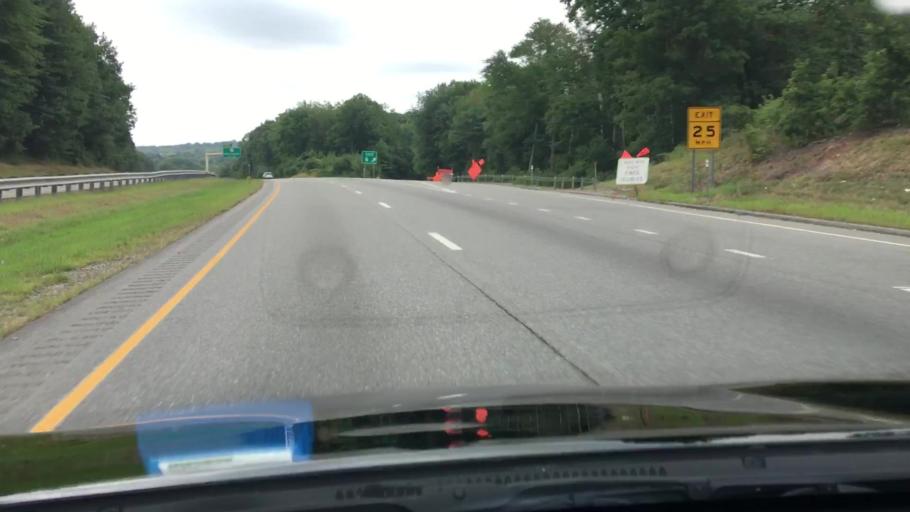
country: US
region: Connecticut
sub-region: New London County
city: Oxoboxo River
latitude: 41.4477
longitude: -72.1181
